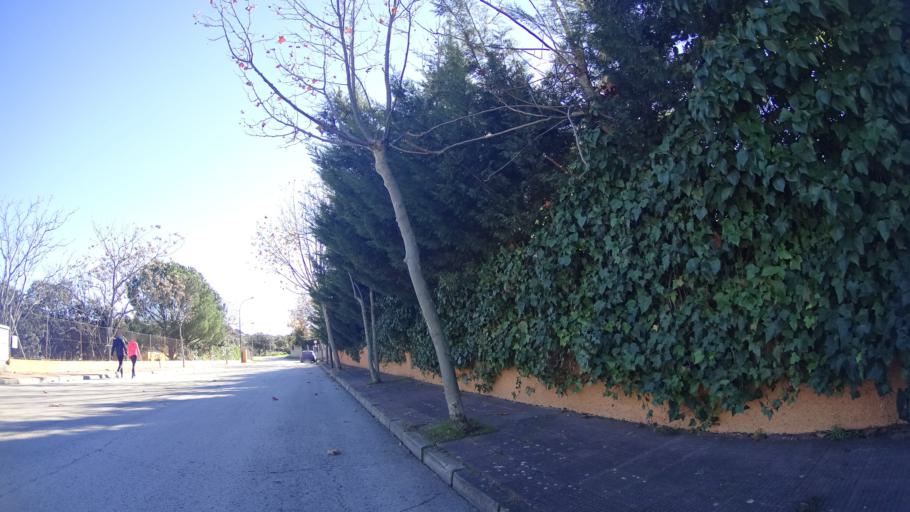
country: ES
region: Madrid
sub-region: Provincia de Madrid
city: Torrelodones
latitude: 40.5947
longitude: -3.9506
